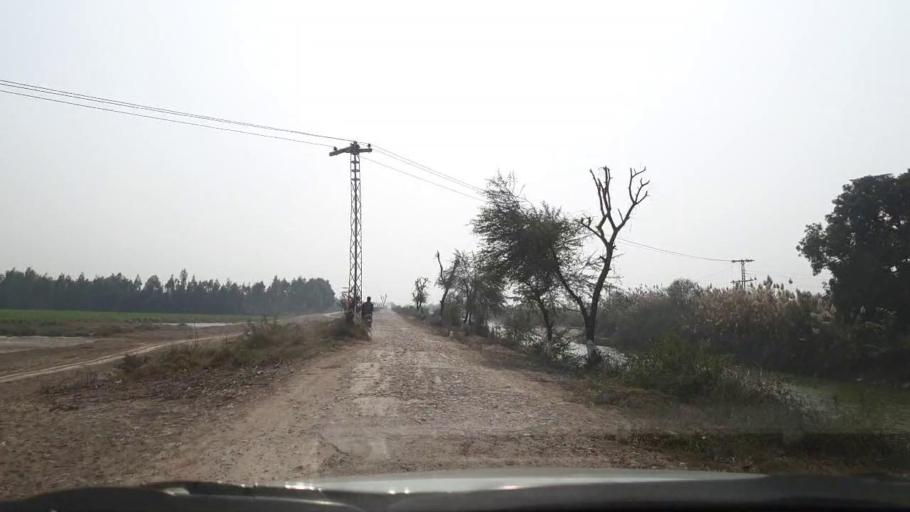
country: PK
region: Sindh
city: Matiari
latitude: 25.6426
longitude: 68.5605
